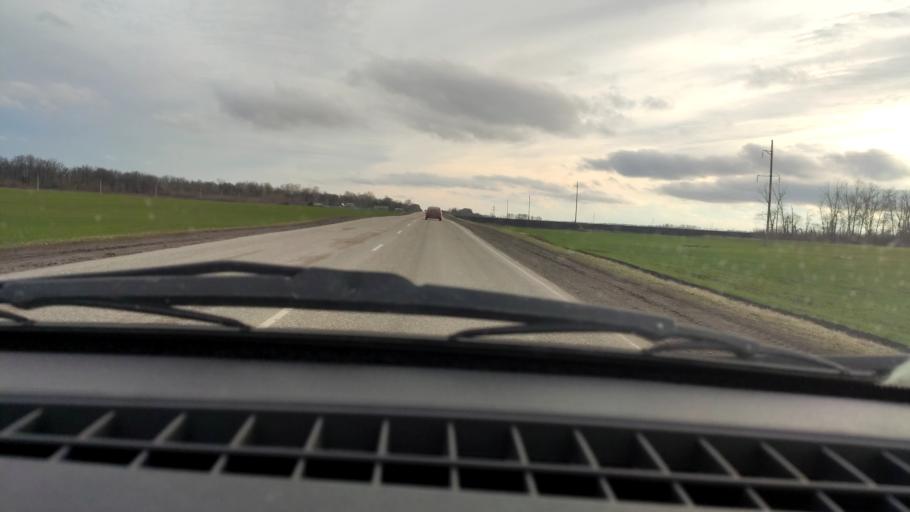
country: RU
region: Bashkortostan
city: Chishmy
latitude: 54.5537
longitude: 55.3350
